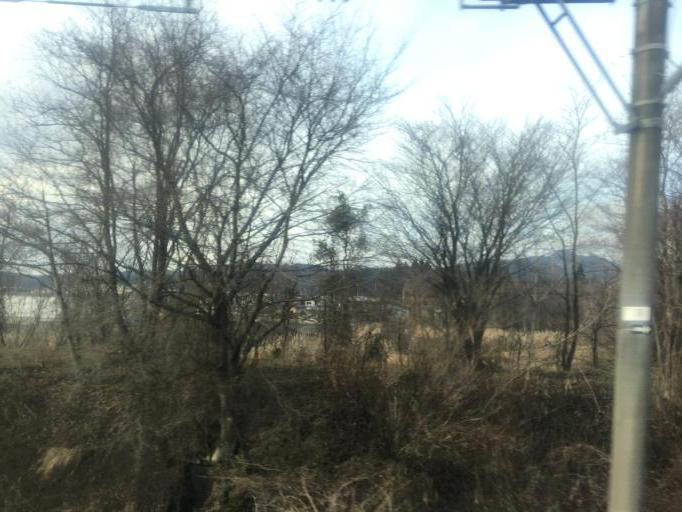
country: JP
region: Akita
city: Odate
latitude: 40.2977
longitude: 140.5665
